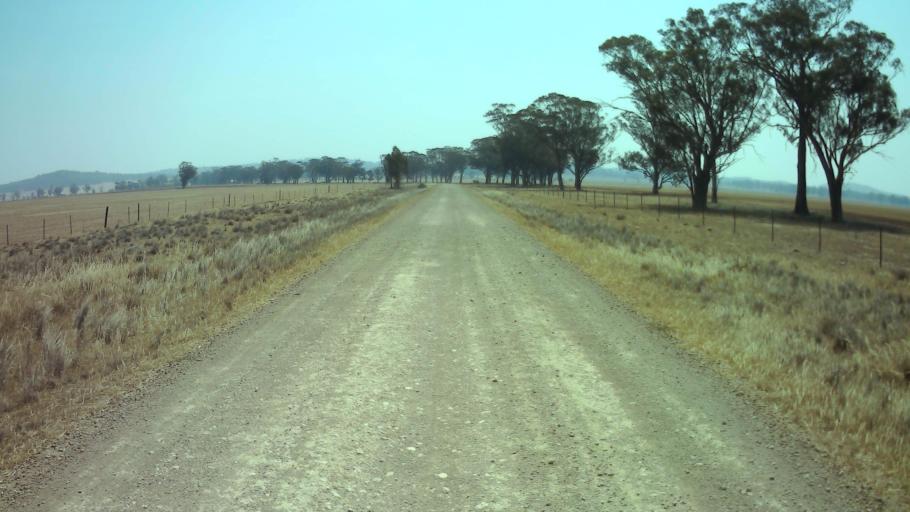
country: AU
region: New South Wales
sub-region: Weddin
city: Grenfell
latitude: -33.6376
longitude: 148.2456
